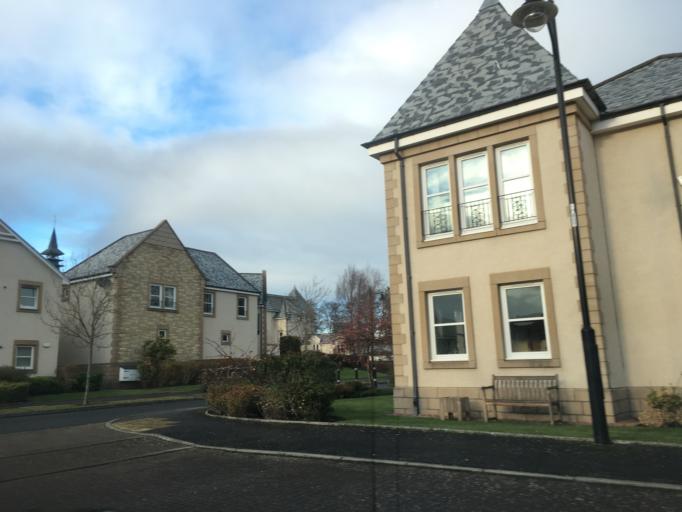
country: GB
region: Scotland
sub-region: Edinburgh
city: Colinton
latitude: 55.9157
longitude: -3.2249
